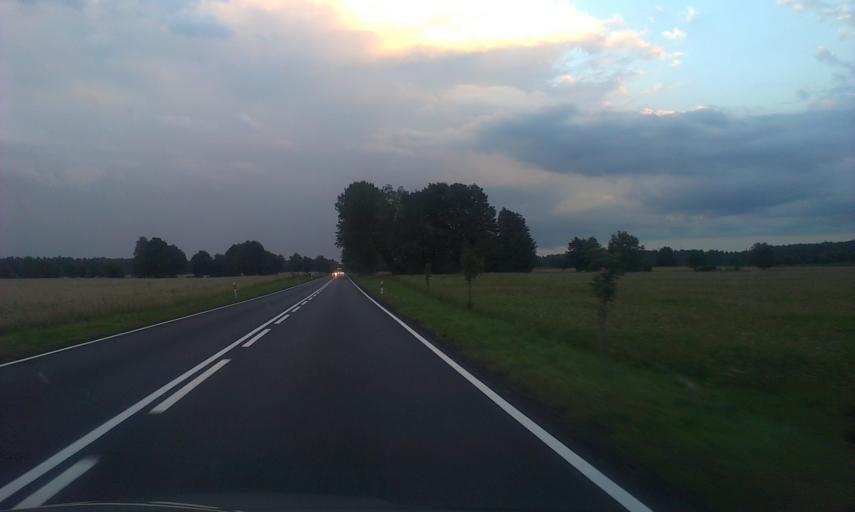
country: PL
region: West Pomeranian Voivodeship
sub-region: Powiat koszalinski
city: Bobolice
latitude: 54.0215
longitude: 16.4778
